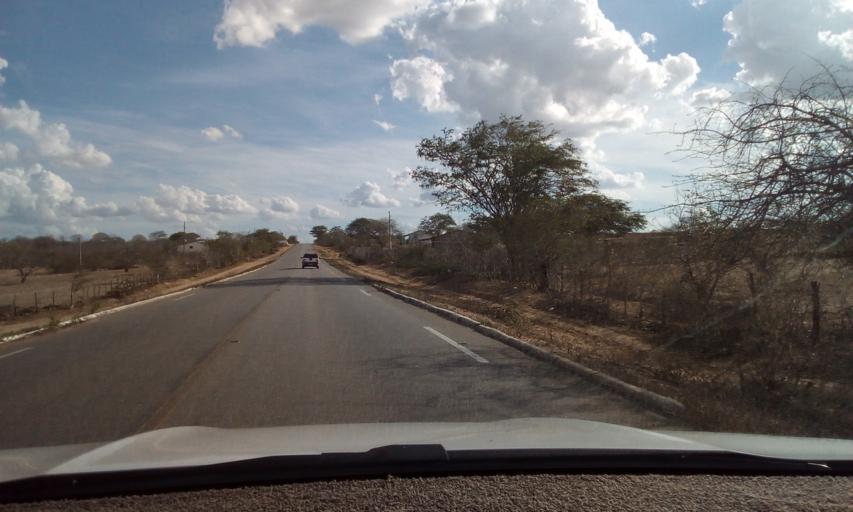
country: BR
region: Paraiba
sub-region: Soledade
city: Soledade
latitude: -6.9248
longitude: -36.3853
